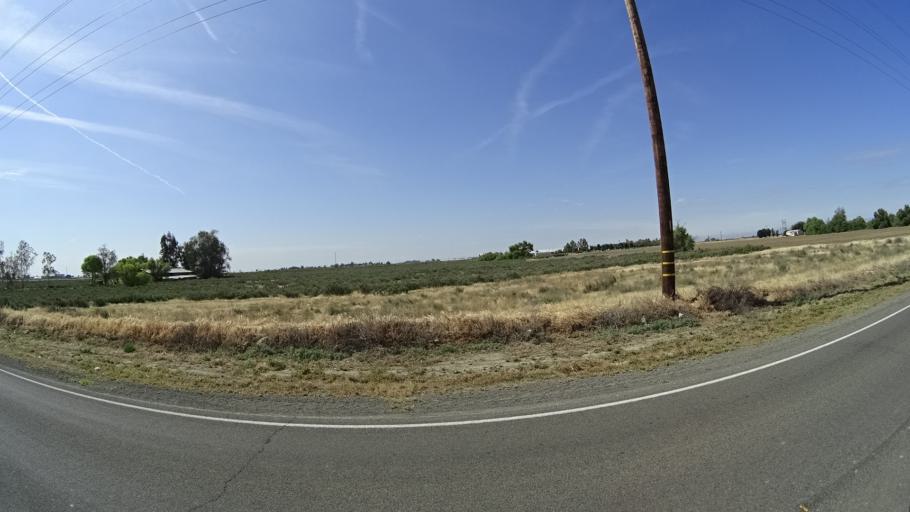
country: US
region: California
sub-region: Kings County
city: Lemoore
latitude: 36.2547
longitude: -119.7953
